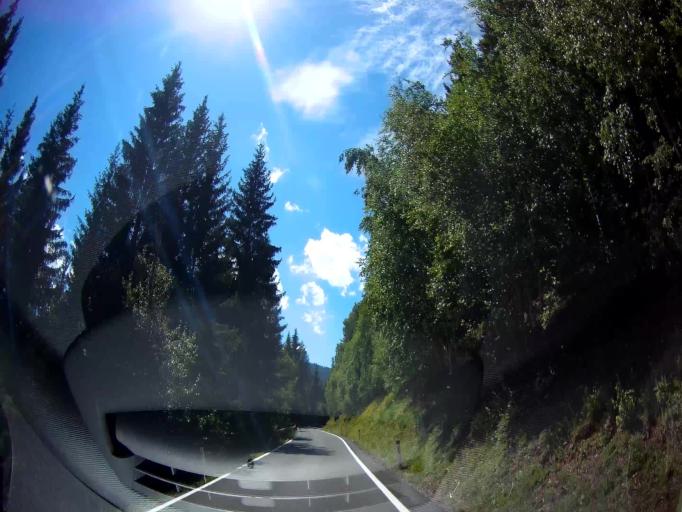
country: AT
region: Carinthia
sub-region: Politischer Bezirk Sankt Veit an der Glan
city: Glodnitz
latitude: 46.9179
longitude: 14.0646
